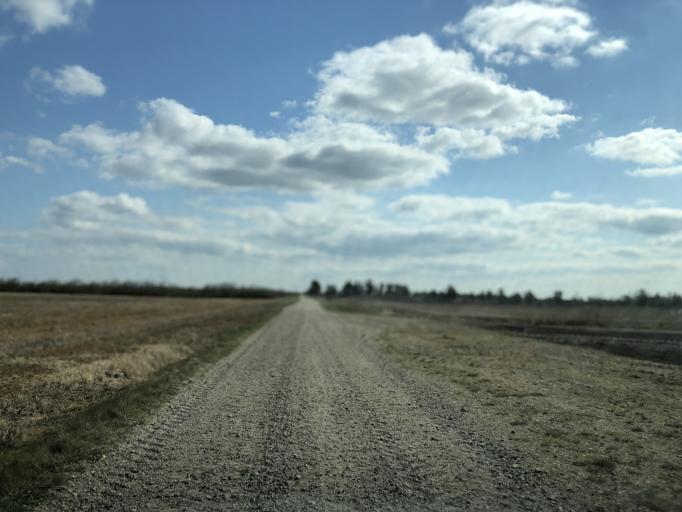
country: DK
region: Central Jutland
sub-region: Holstebro Kommune
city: Ulfborg
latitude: 56.4024
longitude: 8.1868
